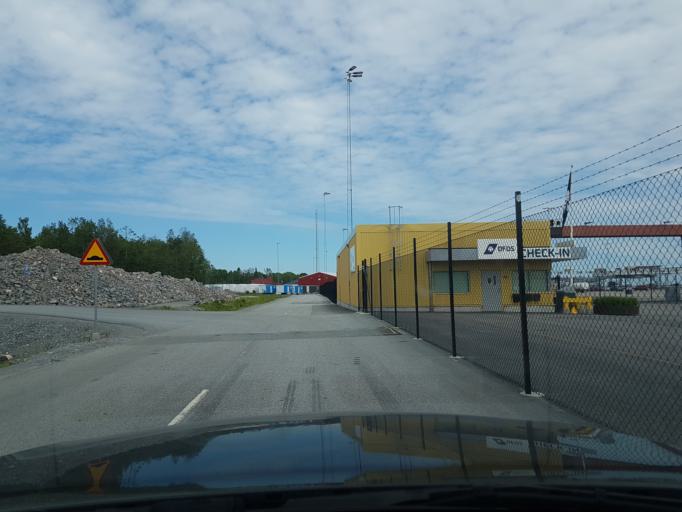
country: SE
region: Stockholm
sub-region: Norrtalje Kommun
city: Bjorko
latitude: 59.7226
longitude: 19.0606
